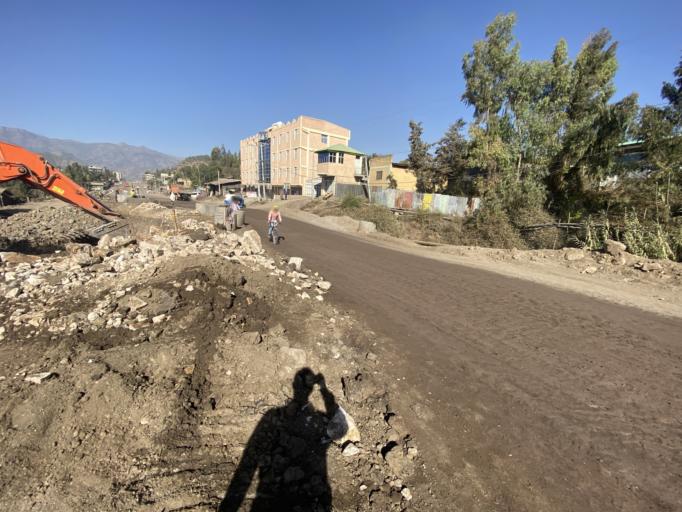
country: ET
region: Amhara
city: Robit
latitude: 11.8255
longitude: 39.5869
